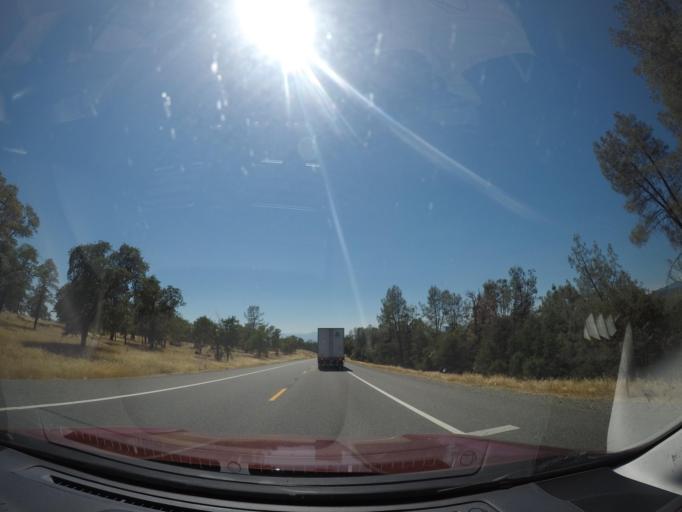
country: US
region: California
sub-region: Shasta County
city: Bella Vista
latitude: 40.6877
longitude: -122.1324
